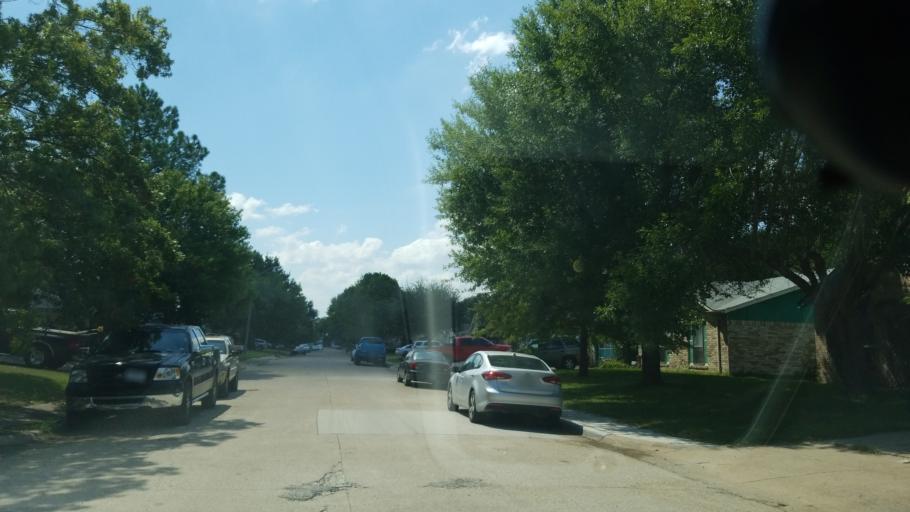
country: US
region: Texas
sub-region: Dallas County
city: Grand Prairie
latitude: 32.7148
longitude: -96.9924
